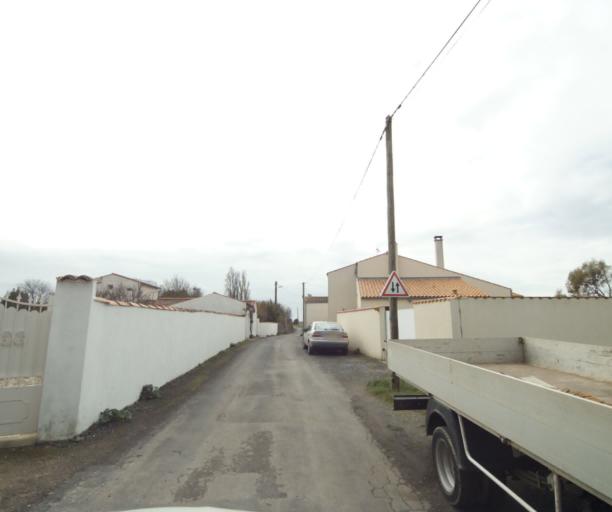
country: FR
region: Poitou-Charentes
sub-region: Departement de la Charente-Maritime
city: Lagord
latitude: 46.1879
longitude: -1.1680
